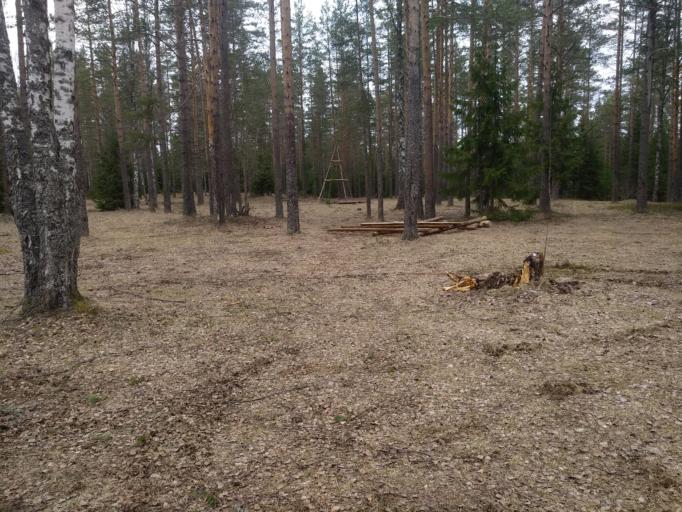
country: RU
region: Leningrad
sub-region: Vsevolzhskij Rajon
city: Vaskelovo
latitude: 60.4434
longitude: 30.3495
